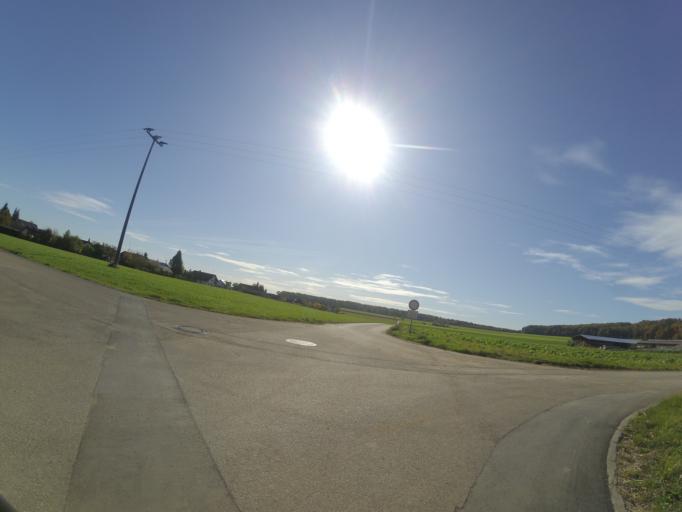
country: DE
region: Baden-Wuerttemberg
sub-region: Tuebingen Region
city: Weidenstetten
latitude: 48.5530
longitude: 9.9885
